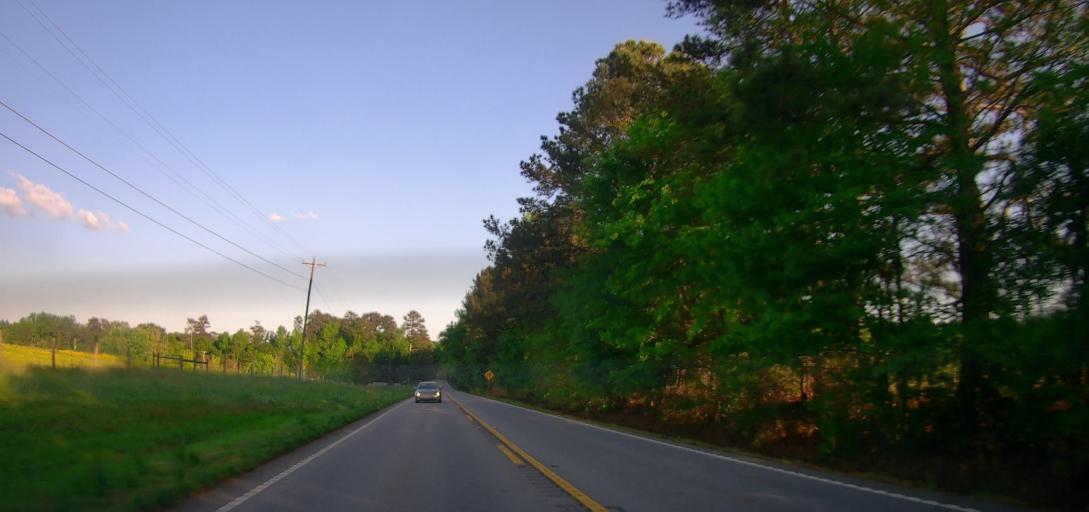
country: US
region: Georgia
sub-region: Walton County
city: Social Circle
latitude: 33.5480
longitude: -83.7331
